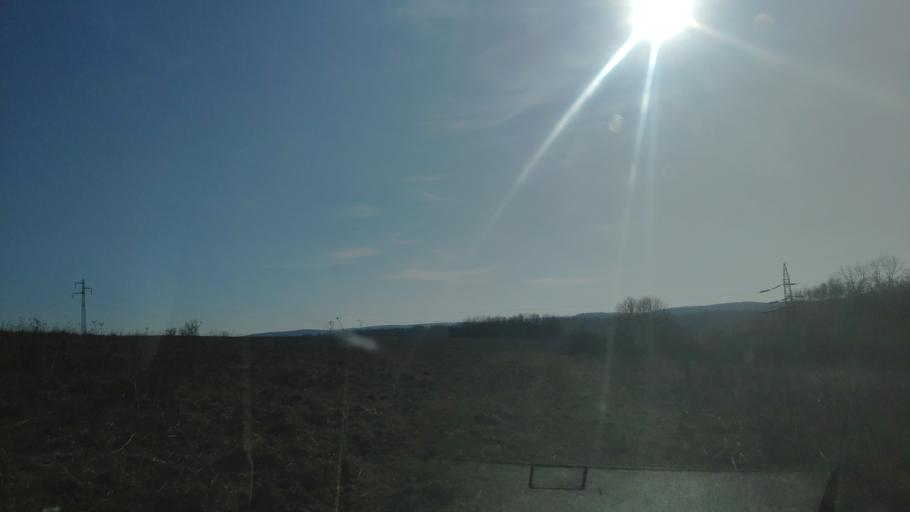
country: SK
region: Banskobystricky
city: Revuca
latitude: 48.5432
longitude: 20.2535
